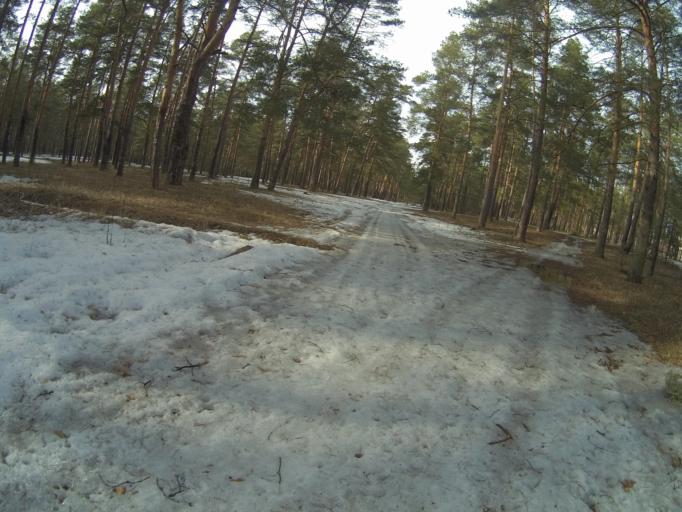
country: RU
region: Vladimir
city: Kommunar
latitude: 56.0844
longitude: 40.4378
